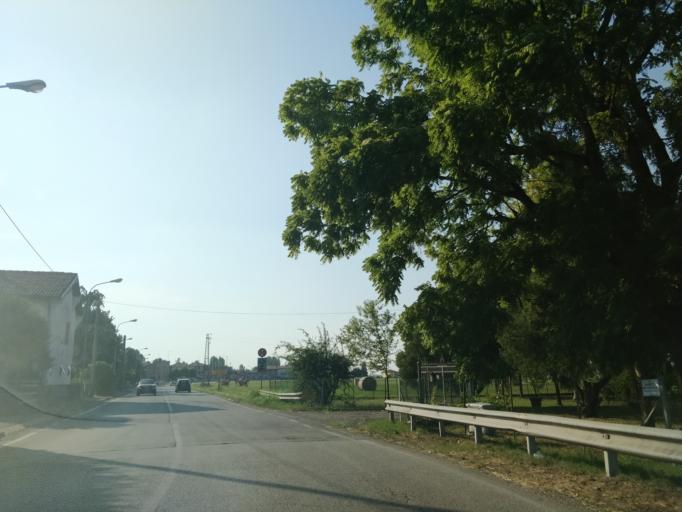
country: IT
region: Emilia-Romagna
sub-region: Provincia di Bologna
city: Castello d'Argile
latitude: 44.6810
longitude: 11.3016
